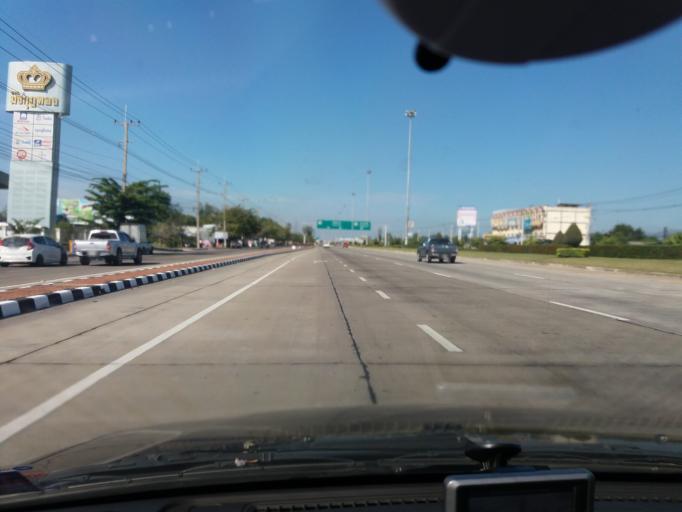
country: TH
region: Suphan Buri
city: Suphan Buri
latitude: 14.4836
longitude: 100.1314
